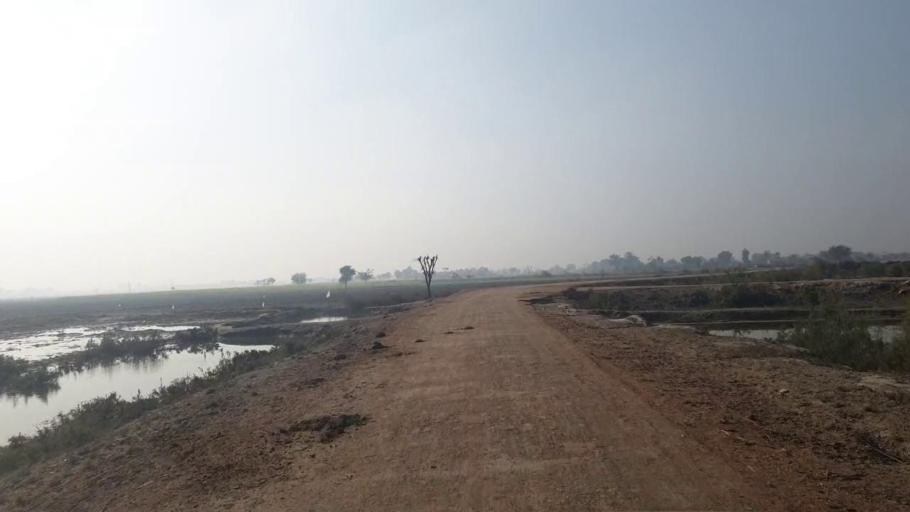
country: PK
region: Sindh
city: Shahdadpur
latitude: 25.9476
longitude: 68.5773
